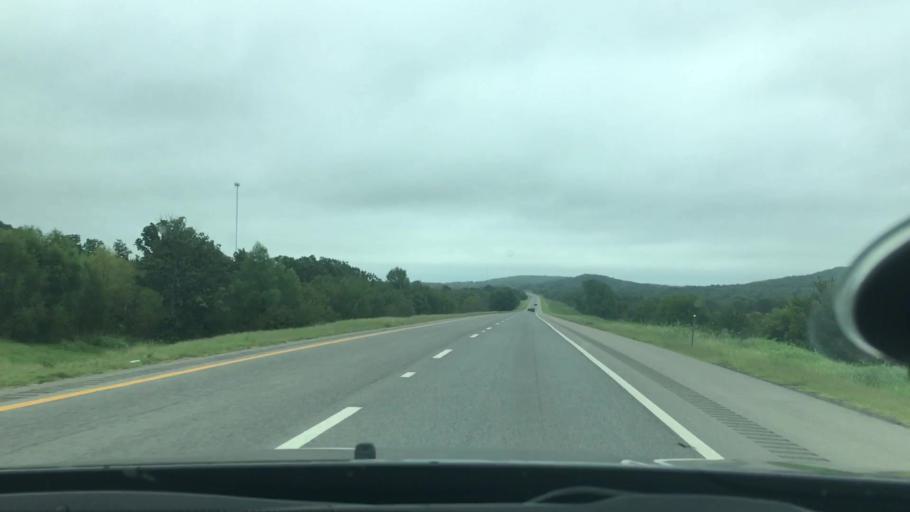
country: US
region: Oklahoma
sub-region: McIntosh County
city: Checotah
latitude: 35.4572
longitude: -95.4228
